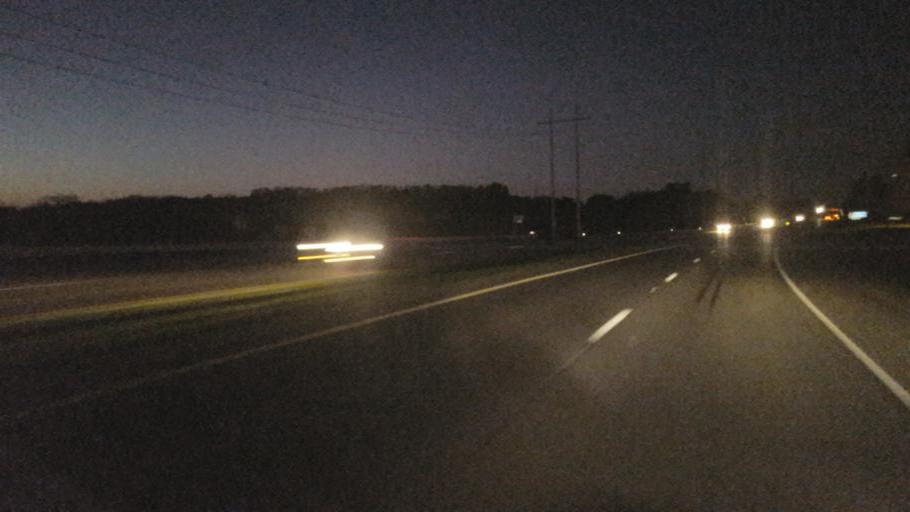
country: US
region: Ohio
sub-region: Pickaway County
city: Circleville
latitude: 39.5946
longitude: -82.9546
